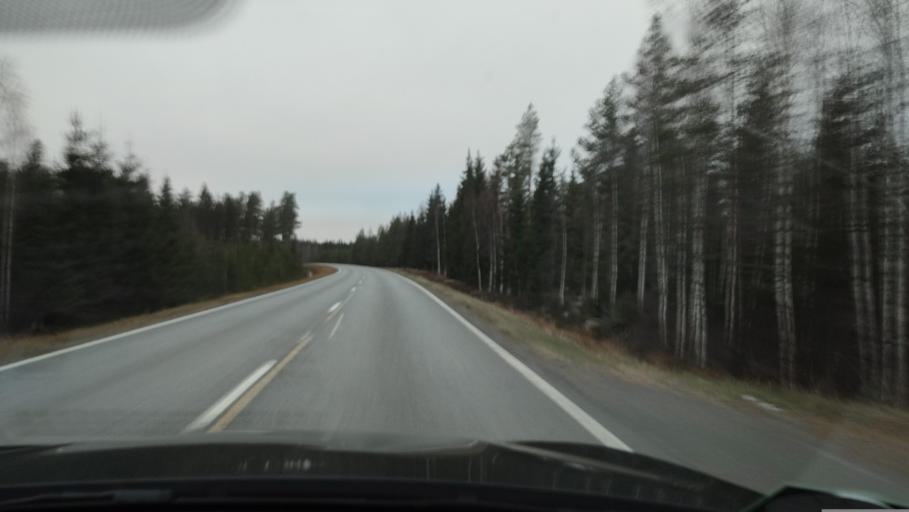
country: FI
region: Southern Ostrobothnia
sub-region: Suupohja
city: Karijoki
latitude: 62.3269
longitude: 21.8581
